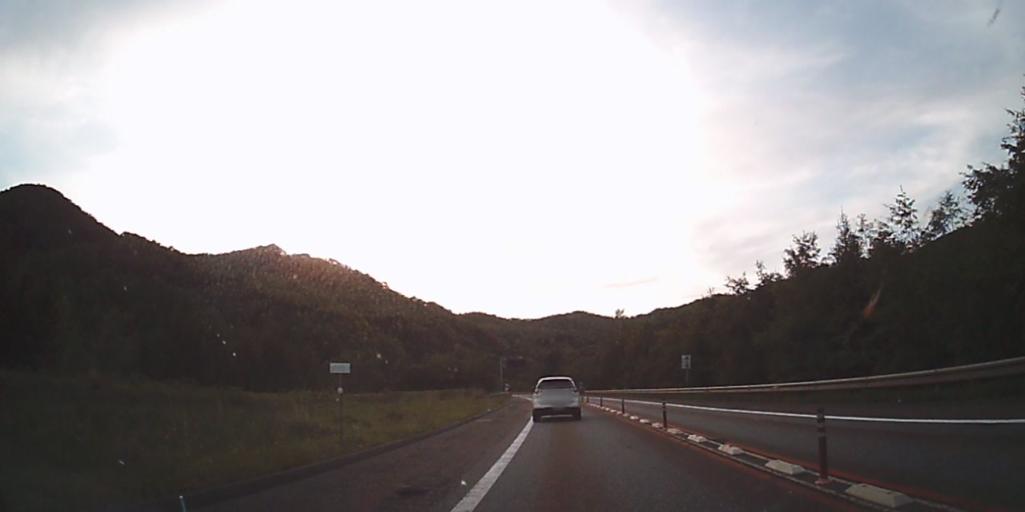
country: JP
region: Hokkaido
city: Date
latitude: 42.5716
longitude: 140.7488
